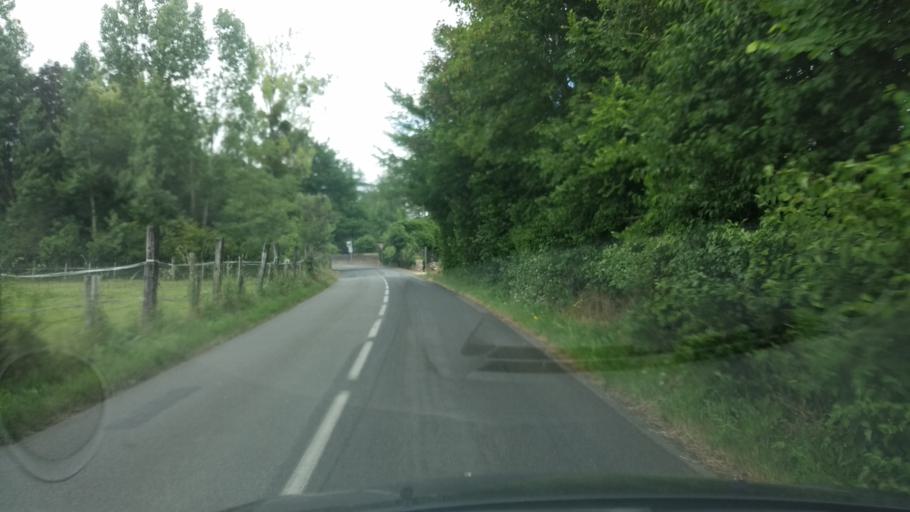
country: FR
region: Poitou-Charentes
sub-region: Departement de la Vienne
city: Vouille
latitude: 46.6356
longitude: 0.1681
